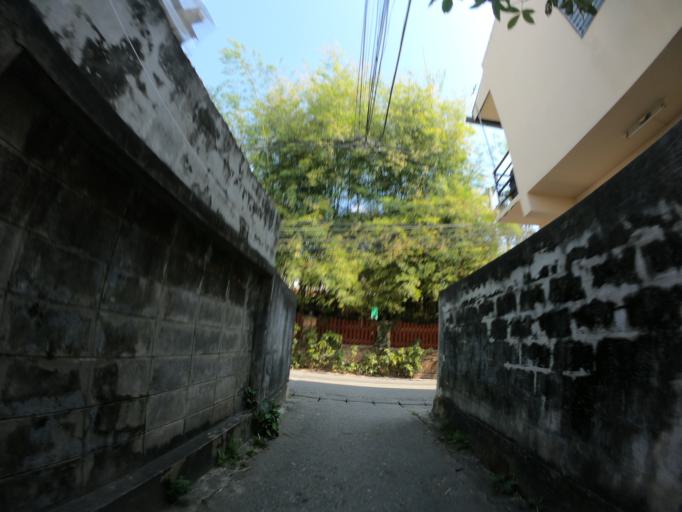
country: TH
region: Chiang Mai
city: Chiang Mai
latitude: 18.7898
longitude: 99.0058
